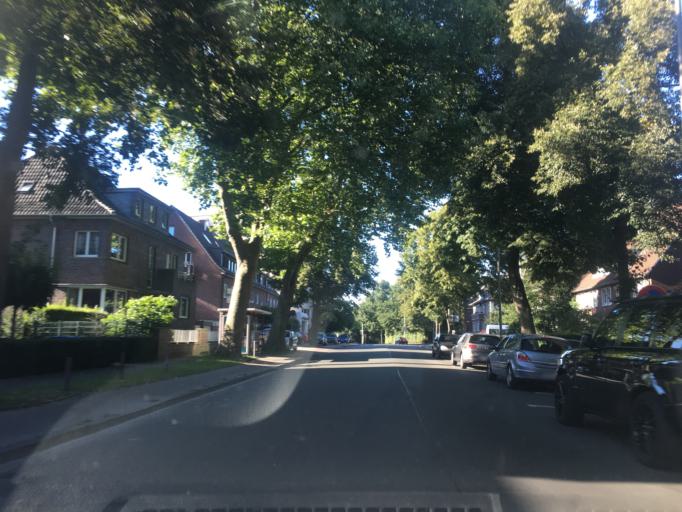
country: DE
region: North Rhine-Westphalia
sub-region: Regierungsbezirk Munster
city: Muenster
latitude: 51.9739
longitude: 7.6404
